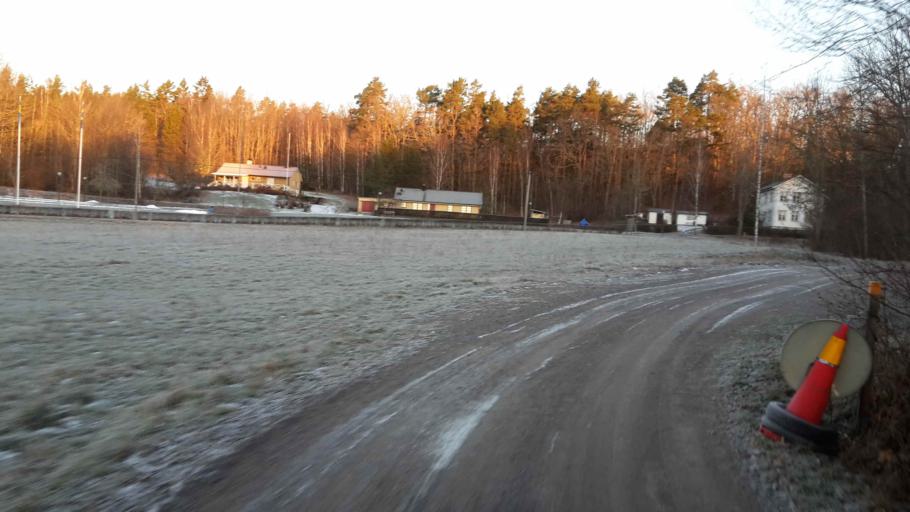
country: SE
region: OEstergoetland
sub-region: Soderkopings Kommun
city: Soederkoeping
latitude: 58.2801
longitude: 16.2165
